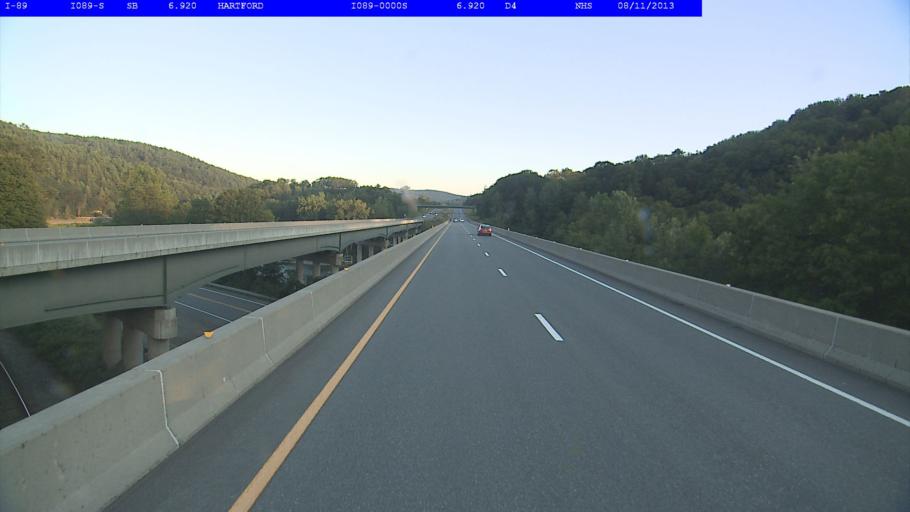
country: US
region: Vermont
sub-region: Windsor County
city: Wilder
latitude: 43.7047
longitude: -72.4125
